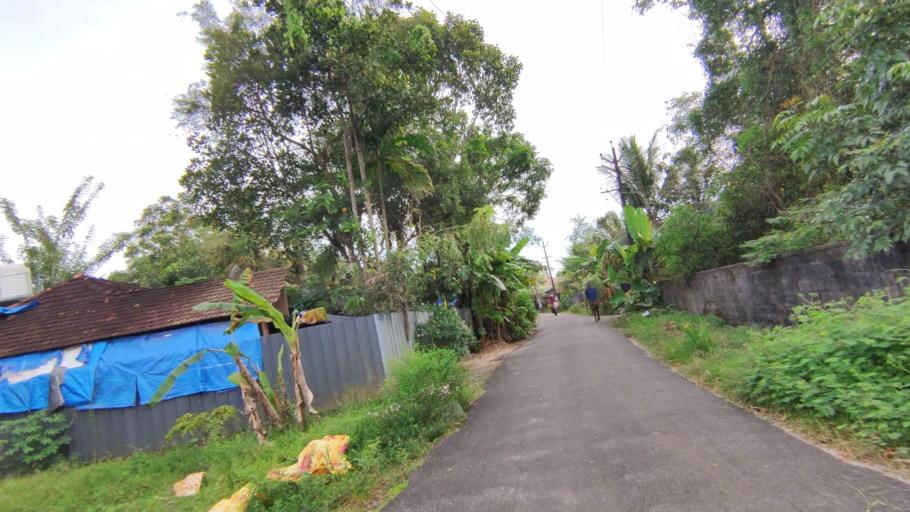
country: IN
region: Kerala
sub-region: Alappuzha
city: Shertallai
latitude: 9.6429
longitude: 76.3398
